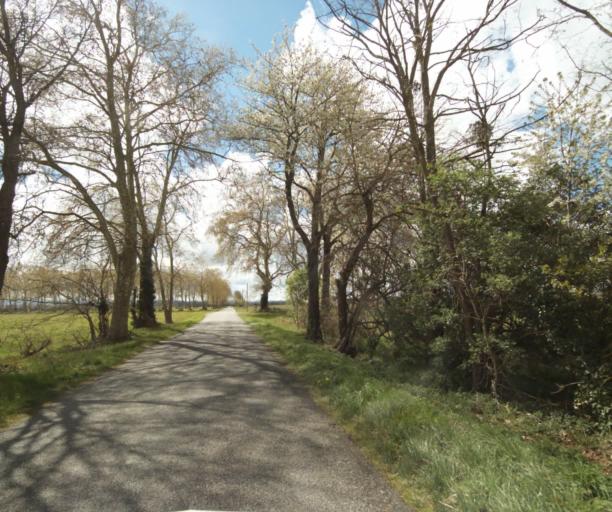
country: FR
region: Midi-Pyrenees
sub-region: Departement de l'Ariege
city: Saverdun
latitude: 43.2586
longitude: 1.6045
